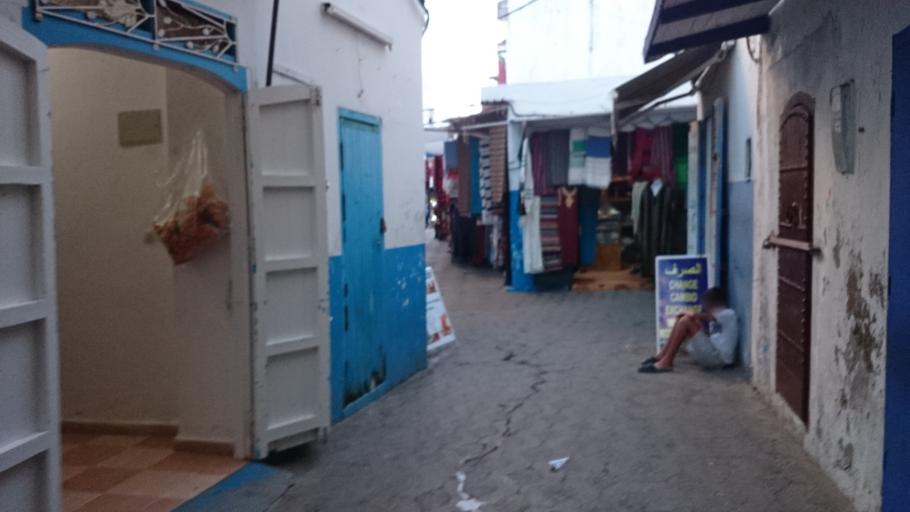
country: MA
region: Tanger-Tetouan
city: Asilah
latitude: 35.4651
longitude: -6.0385
